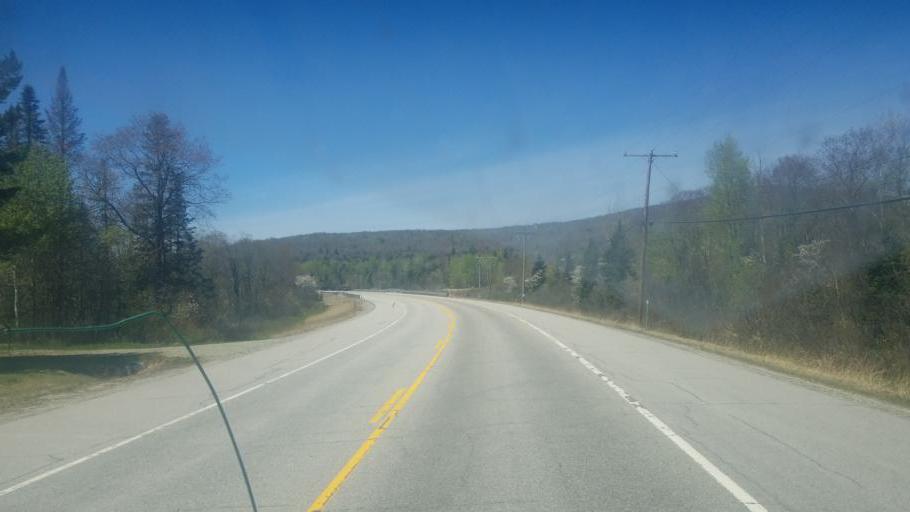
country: US
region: New Hampshire
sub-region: Coos County
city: Jefferson
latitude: 44.2690
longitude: -71.4694
